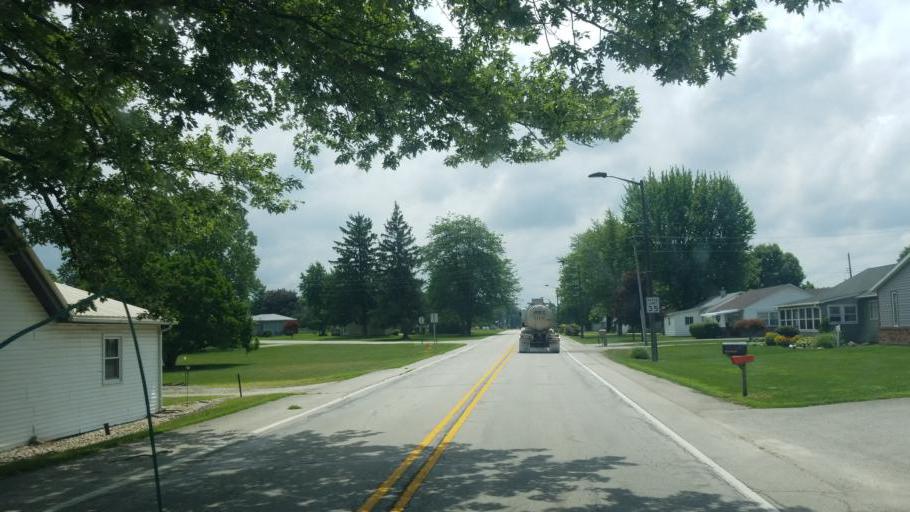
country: US
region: Indiana
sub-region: Huntington County
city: Warren
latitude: 40.6787
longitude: -85.4214
